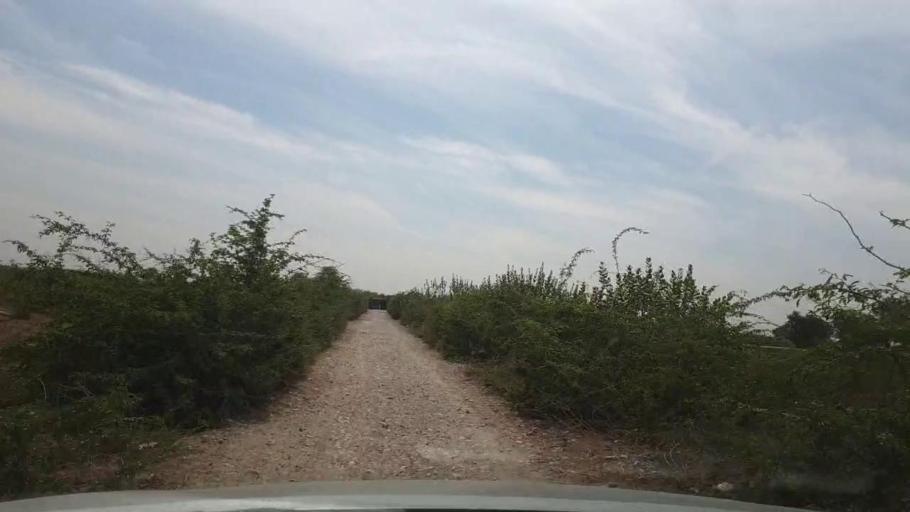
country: PK
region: Sindh
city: Nabisar
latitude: 25.0733
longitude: 69.5987
